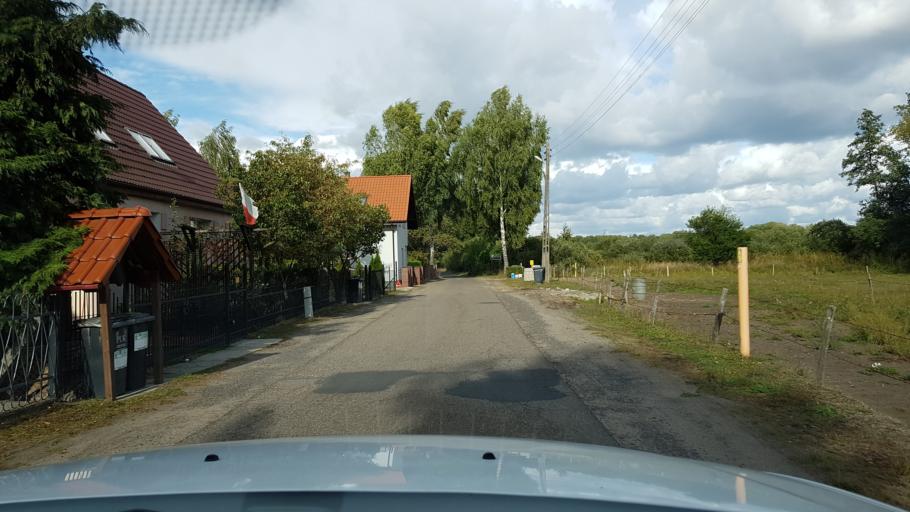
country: PL
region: West Pomeranian Voivodeship
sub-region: Powiat gryfinski
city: Gryfino
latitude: 53.2965
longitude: 14.5041
